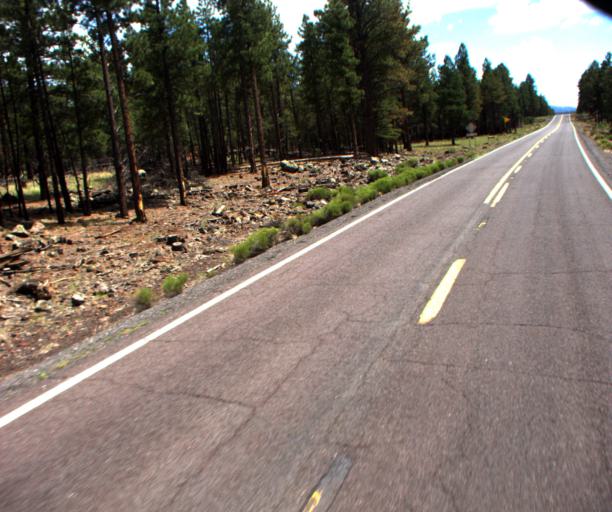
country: US
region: Arizona
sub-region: Coconino County
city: Parks
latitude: 35.4588
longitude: -111.7774
